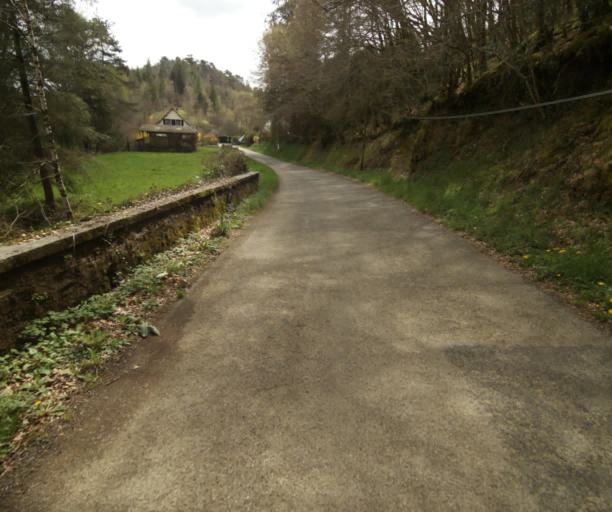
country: FR
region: Limousin
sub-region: Departement de la Correze
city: Laguenne
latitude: 45.2296
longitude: 1.8540
